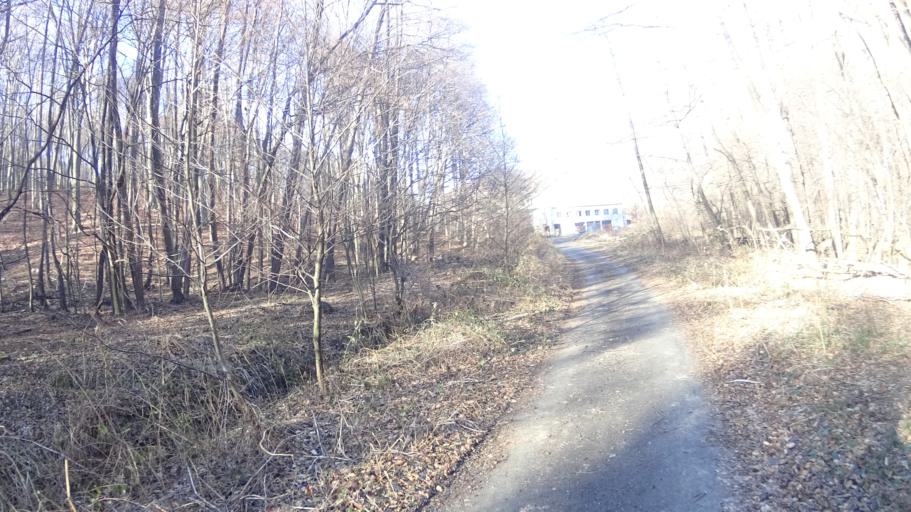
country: HU
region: Heves
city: Paradsasvar
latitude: 47.8805
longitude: 19.9635
